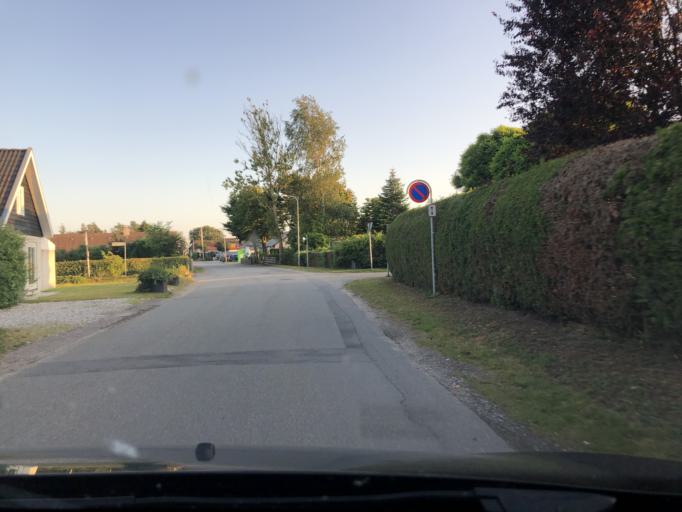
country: DK
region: South Denmark
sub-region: Fredericia Kommune
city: Fredericia
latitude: 55.6320
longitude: 9.7407
